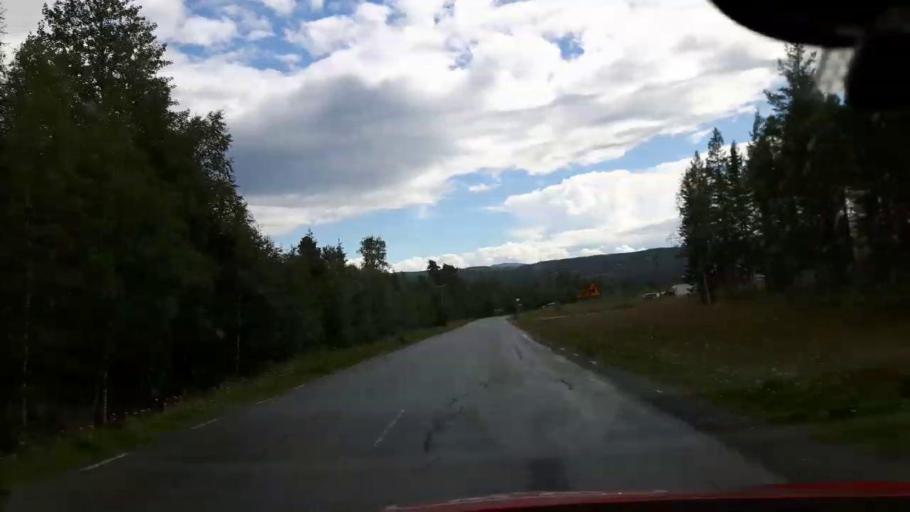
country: SE
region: Jaemtland
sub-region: Are Kommun
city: Are
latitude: 63.3222
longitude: 13.2325
